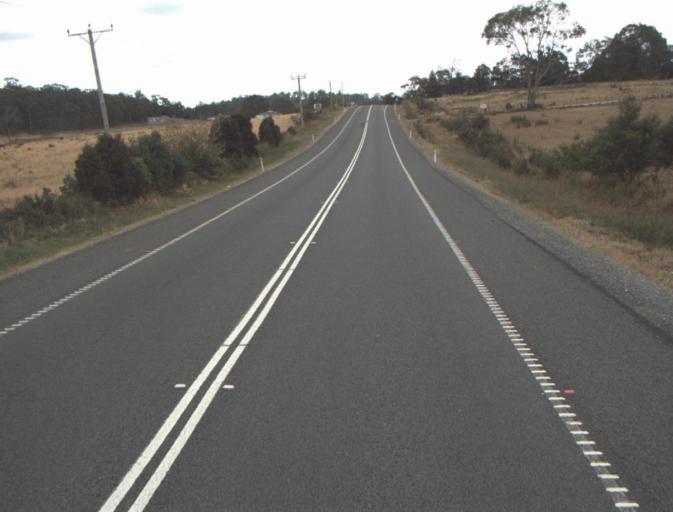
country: AU
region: Tasmania
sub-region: Launceston
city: Mayfield
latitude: -41.2531
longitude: 147.0231
